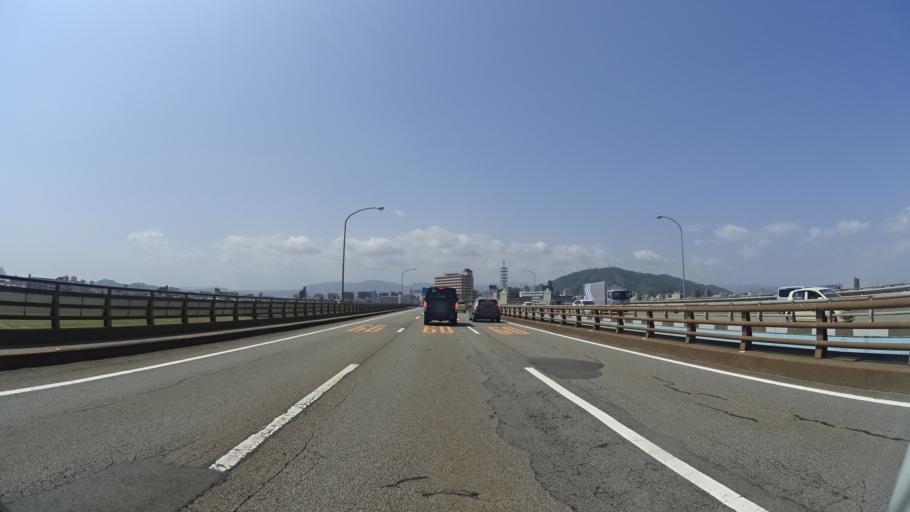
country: JP
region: Tokushima
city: Tokushima-shi
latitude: 34.0870
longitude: 134.5664
